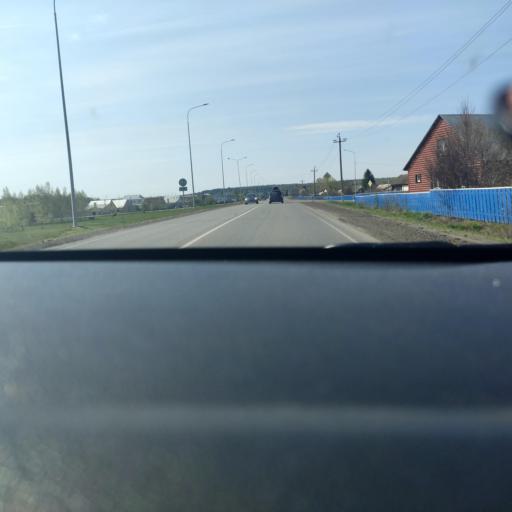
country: RU
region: Tatarstan
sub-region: Alekseyevskiy Rayon
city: Alekseyevskoye
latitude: 55.3023
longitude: 50.1304
